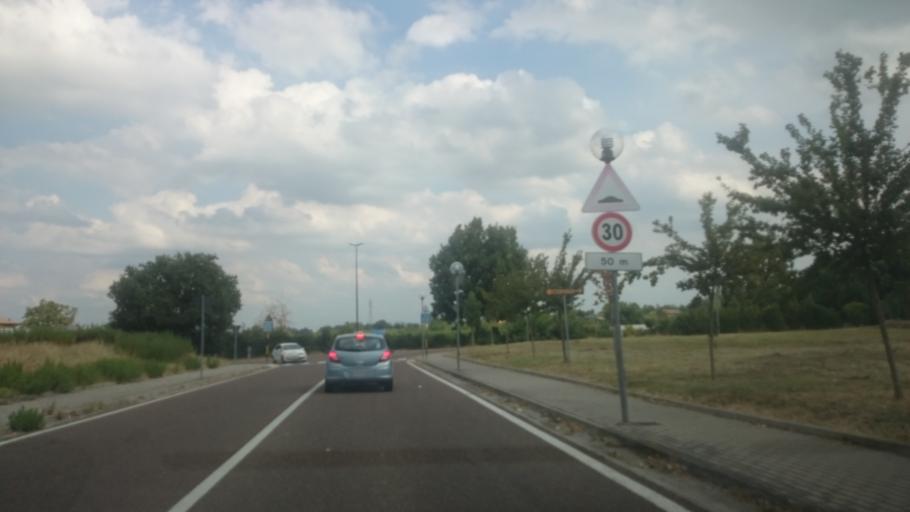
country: IT
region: Emilia-Romagna
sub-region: Provincia di Reggio Emilia
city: Casalgrande
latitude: 44.5878
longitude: 10.7458
